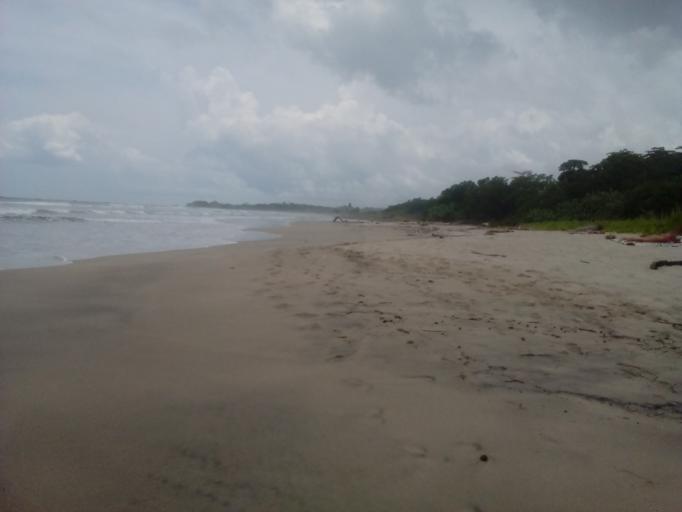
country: CR
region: Guanacaste
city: Samara
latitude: 9.9348
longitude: -85.6653
